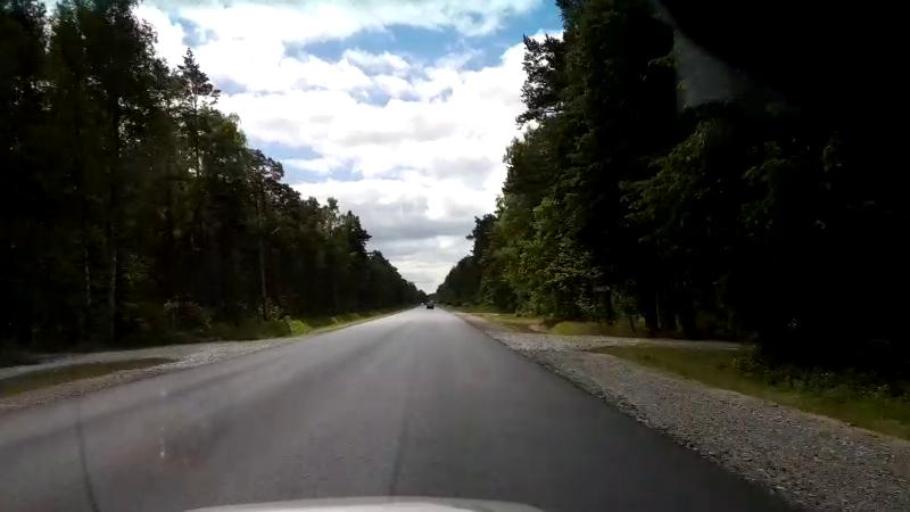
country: LV
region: Salacgrivas
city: Salacgriva
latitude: 57.8051
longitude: 24.3488
